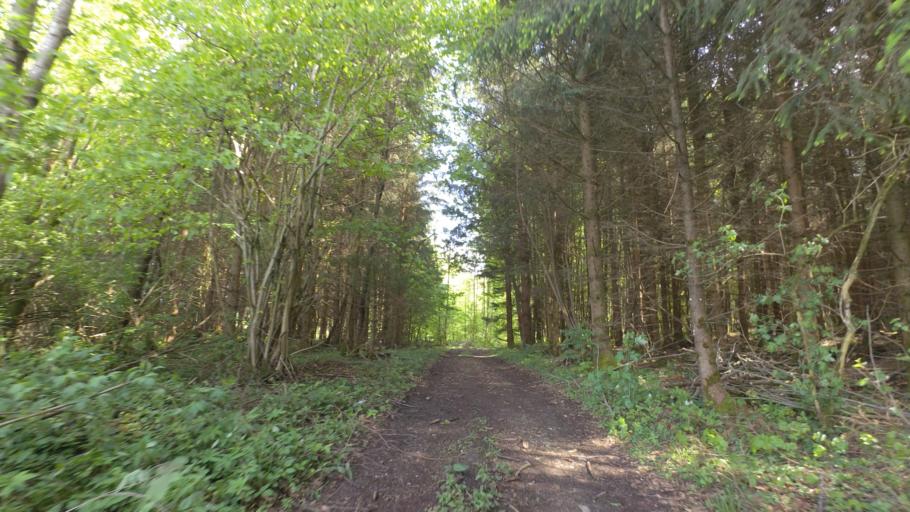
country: DE
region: Bavaria
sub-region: Upper Bavaria
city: Grabenstatt
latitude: 47.8510
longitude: 12.5727
